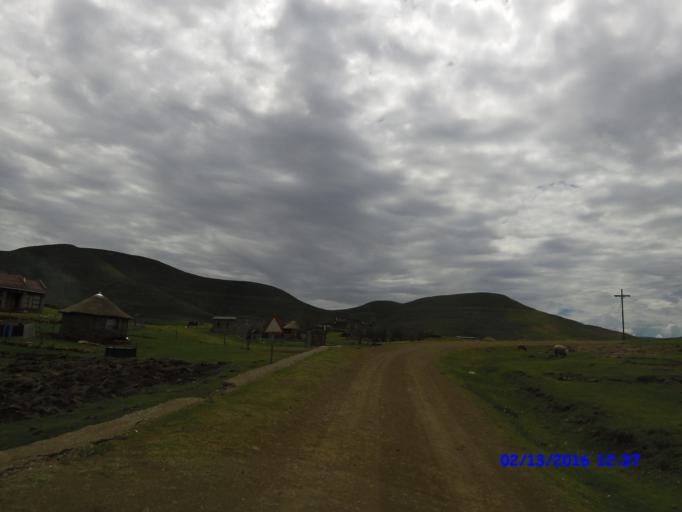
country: LS
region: Maseru
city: Nako
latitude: -29.8381
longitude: 28.0248
